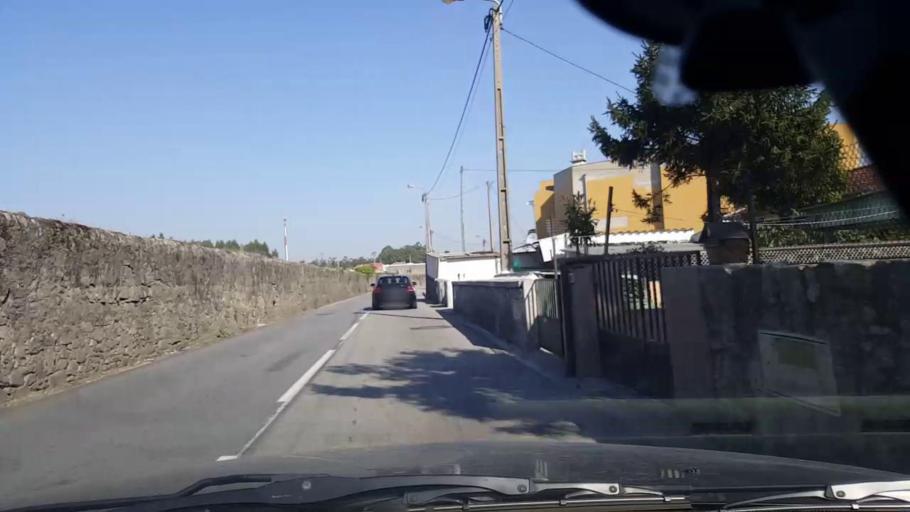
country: PT
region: Porto
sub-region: Vila do Conde
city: Arvore
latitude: 41.3336
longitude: -8.6818
